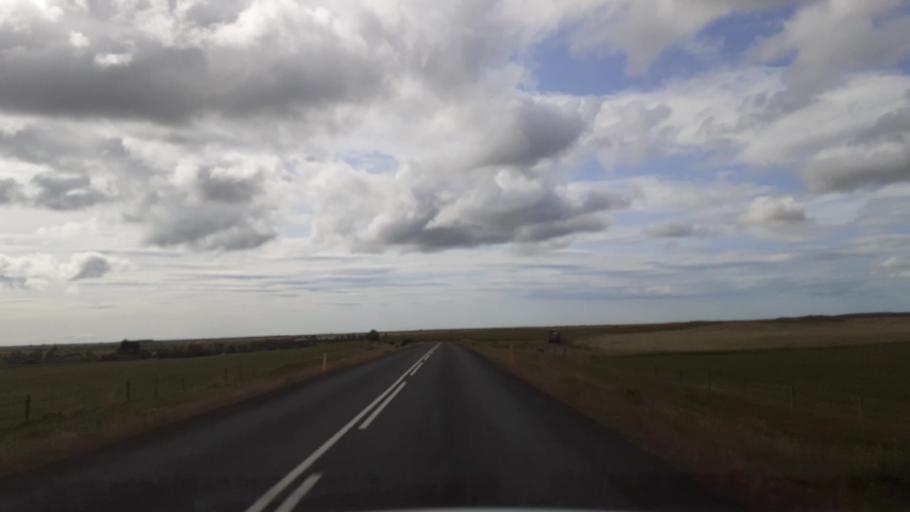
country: IS
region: South
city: Vestmannaeyjar
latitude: 63.8355
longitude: -20.4174
